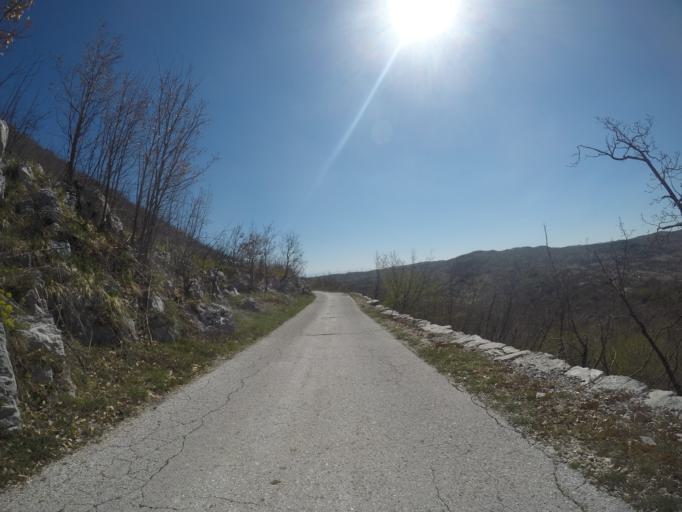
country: ME
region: Cetinje
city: Cetinje
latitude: 42.5285
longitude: 18.9577
